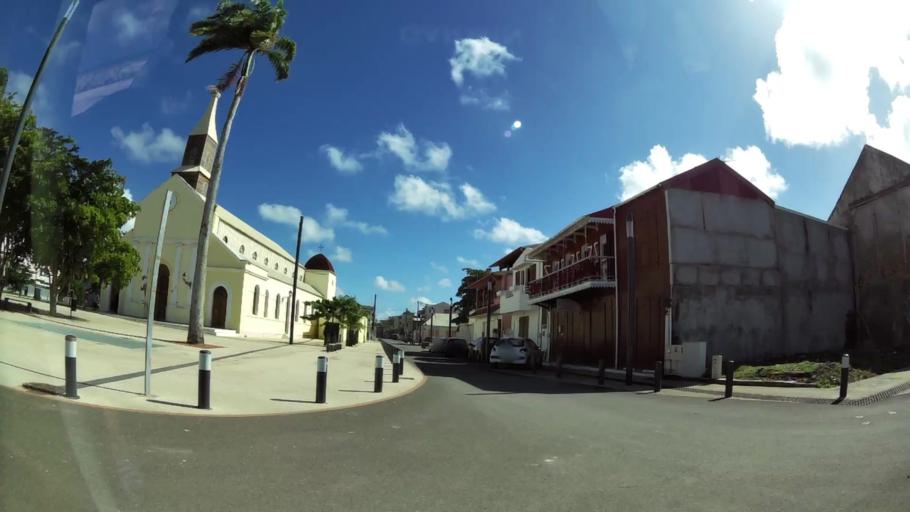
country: GP
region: Guadeloupe
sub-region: Guadeloupe
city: Port-Louis
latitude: 16.4176
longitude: -61.5333
